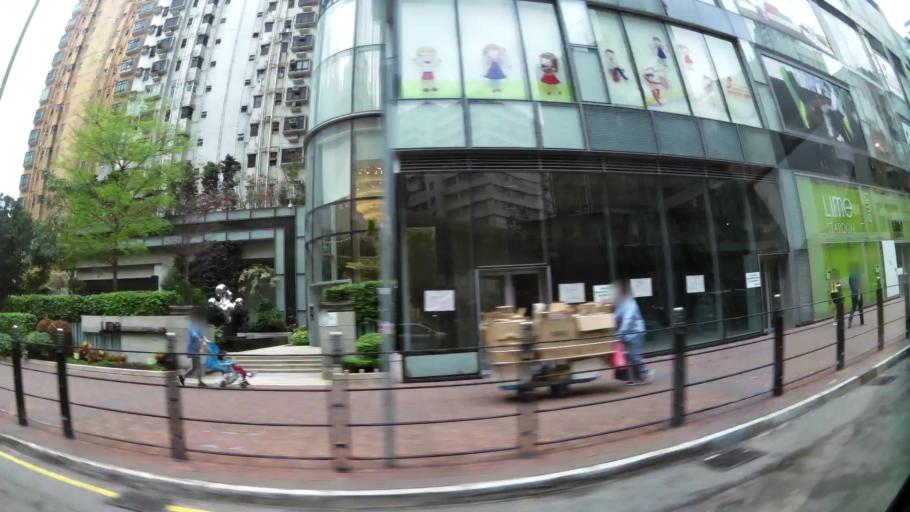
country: HK
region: Sham Shui Po
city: Sham Shui Po
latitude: 22.3210
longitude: 114.1653
